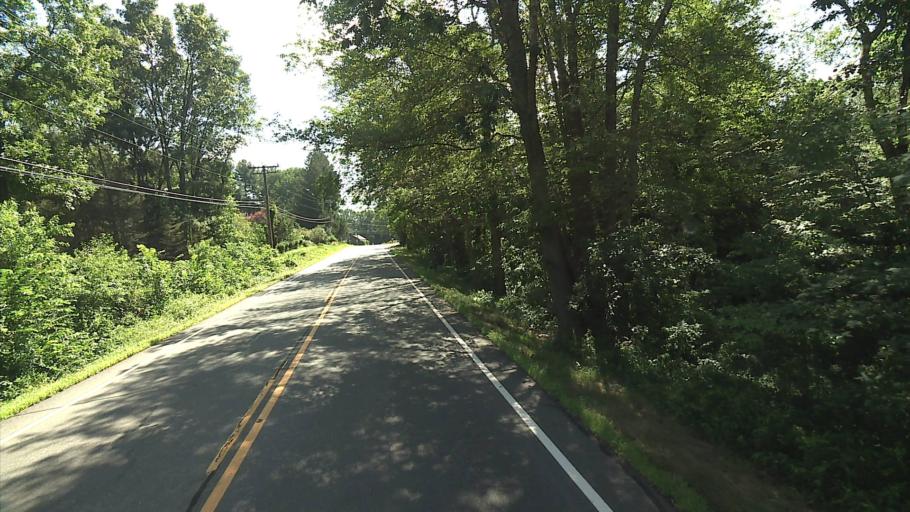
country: US
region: Connecticut
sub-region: Windham County
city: Plainfield Village
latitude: 41.7095
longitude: -72.0243
